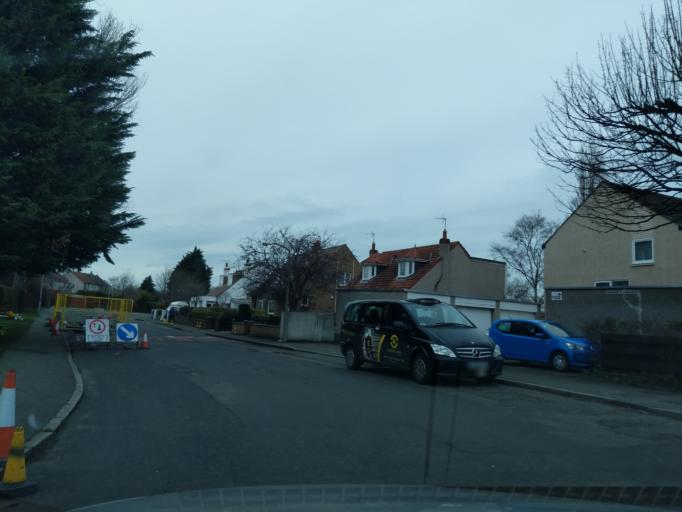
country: GB
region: Scotland
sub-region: Edinburgh
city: Colinton
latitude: 55.9360
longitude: -3.2842
